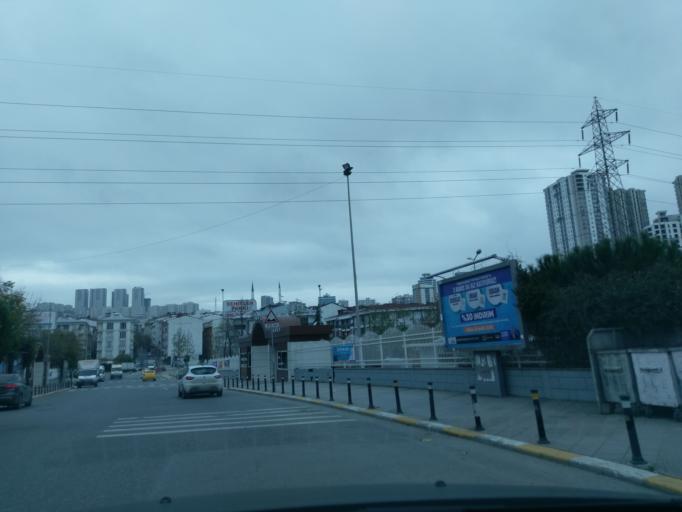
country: TR
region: Istanbul
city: Esenyurt
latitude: 41.0195
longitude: 28.6685
